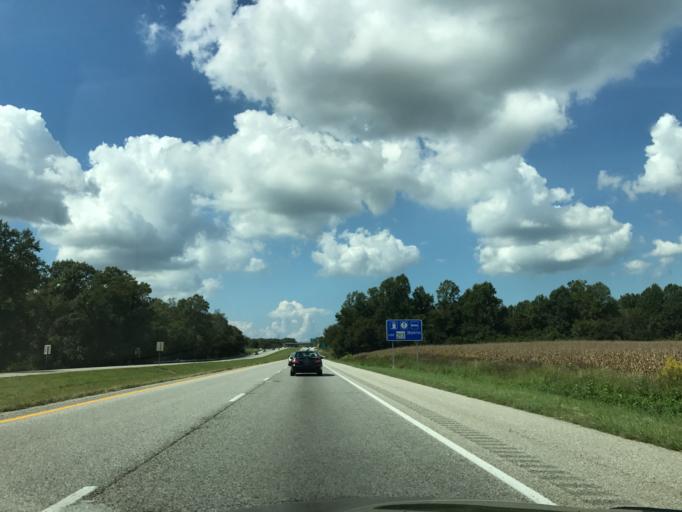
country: US
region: Maryland
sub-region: Queen Anne's County
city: Centreville
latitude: 39.0158
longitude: -76.0642
